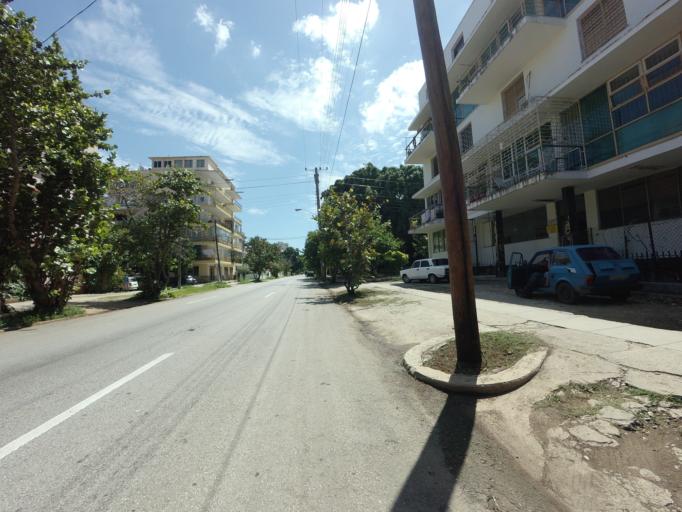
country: CU
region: La Habana
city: Havana
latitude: 23.1351
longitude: -82.4042
